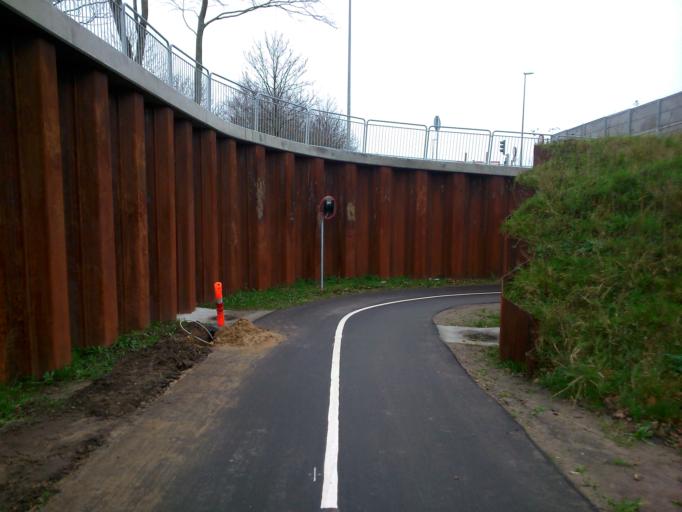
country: DK
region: Central Jutland
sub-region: Herning Kommune
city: Snejbjerg
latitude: 56.1569
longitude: 8.9260
